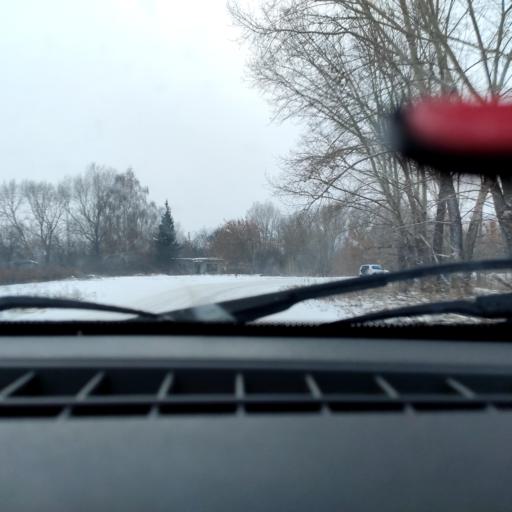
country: RU
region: Bashkortostan
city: Blagoveshchensk
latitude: 54.9055
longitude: 56.0106
